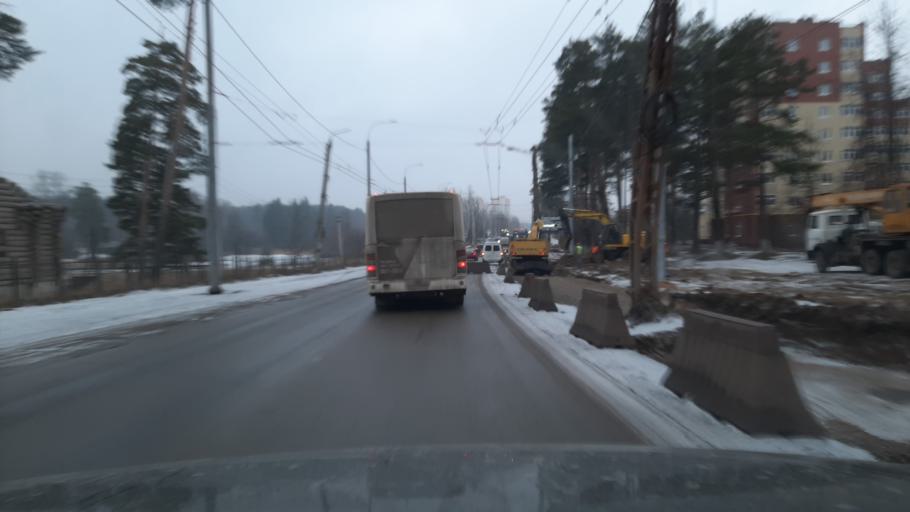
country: RU
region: Ivanovo
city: Kokhma
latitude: 56.9354
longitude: 41.0710
